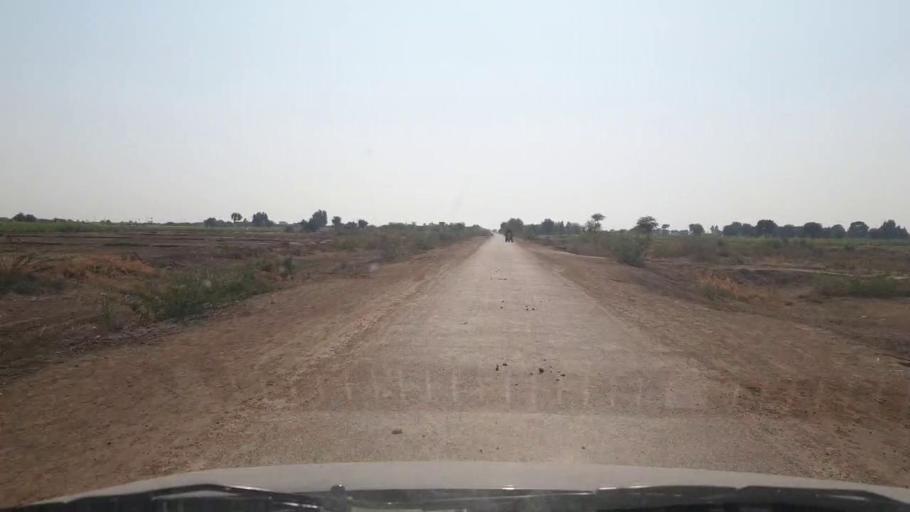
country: PK
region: Sindh
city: Samaro
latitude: 25.1857
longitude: 69.3384
